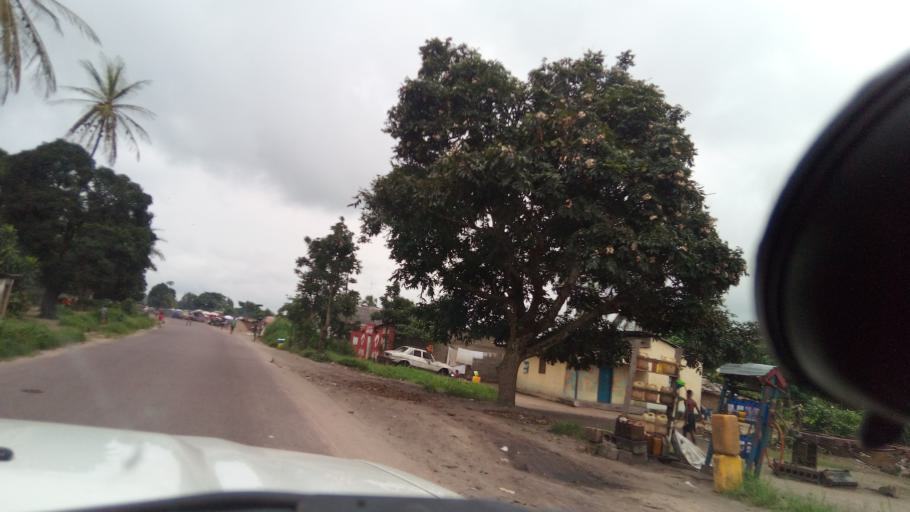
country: CD
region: Bas-Congo
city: Kasangulu
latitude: -4.8257
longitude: 15.1807
